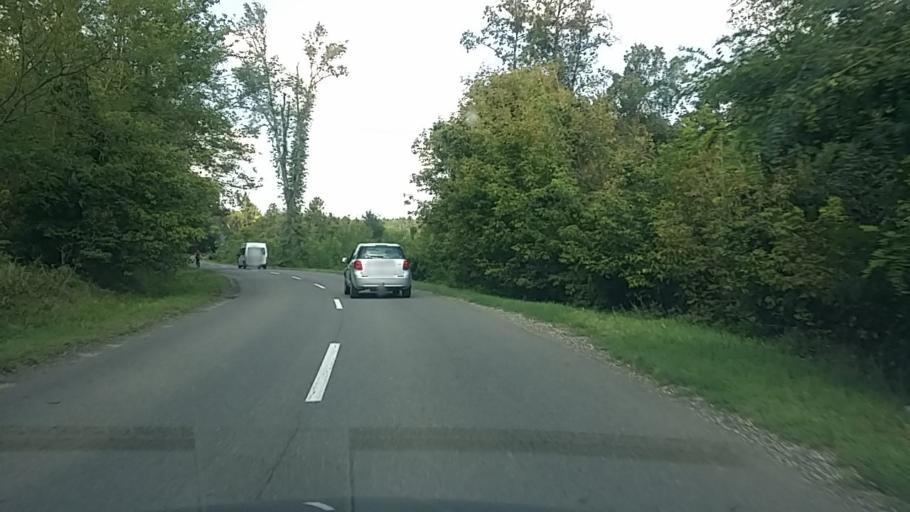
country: HU
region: Bacs-Kiskun
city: Tiszaalpar
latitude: 46.8411
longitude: 19.9784
